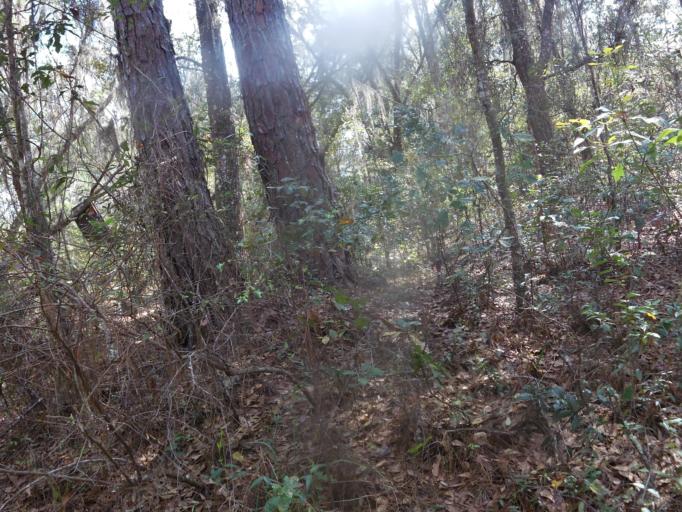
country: US
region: Florida
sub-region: Putnam County
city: Interlachen
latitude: 29.7649
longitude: -81.8452
